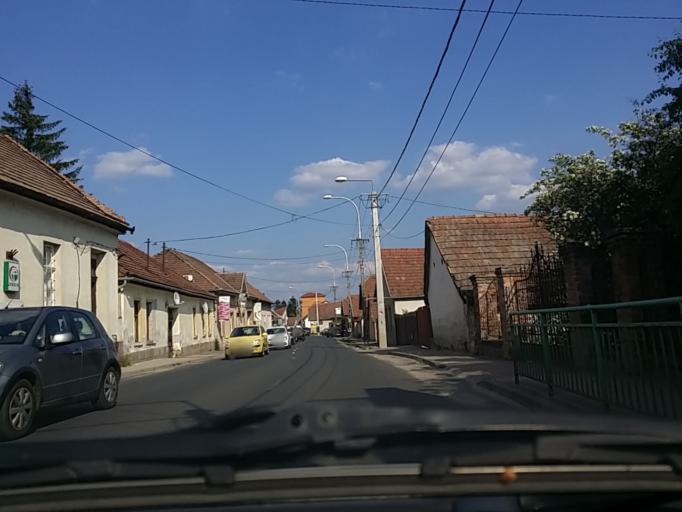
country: HU
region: Pest
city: Nagykovacsi
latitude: 47.6489
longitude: 19.0170
